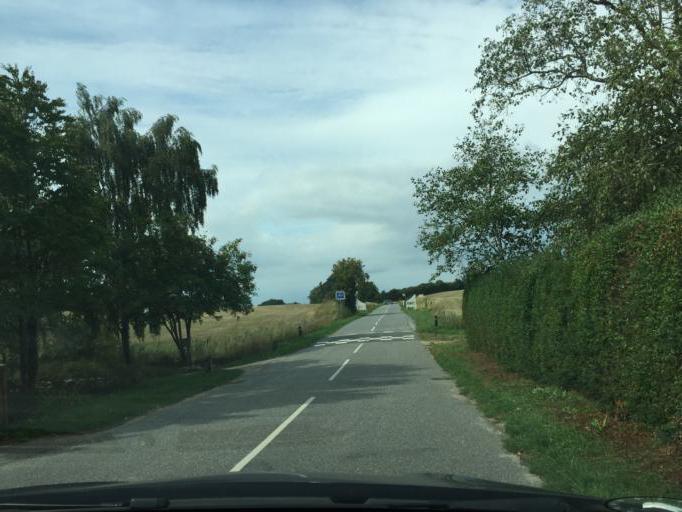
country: DK
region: South Denmark
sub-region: Assens Kommune
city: Vissenbjerg
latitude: 55.3942
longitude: 10.1798
